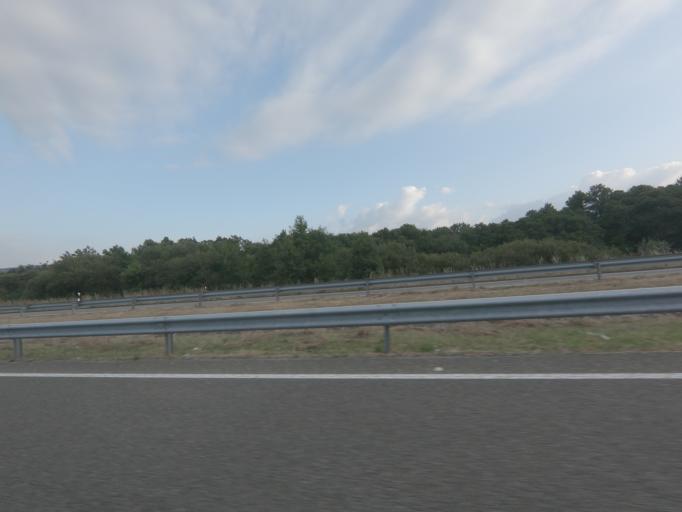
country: ES
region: Galicia
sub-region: Provincia de Ourense
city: Allariz
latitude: 42.2081
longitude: -7.8089
